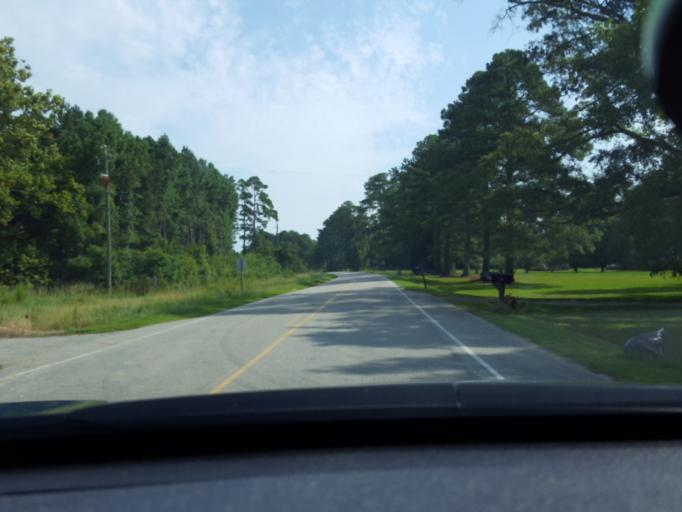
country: US
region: North Carolina
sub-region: Washington County
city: Plymouth
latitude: 35.8766
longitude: -76.7157
